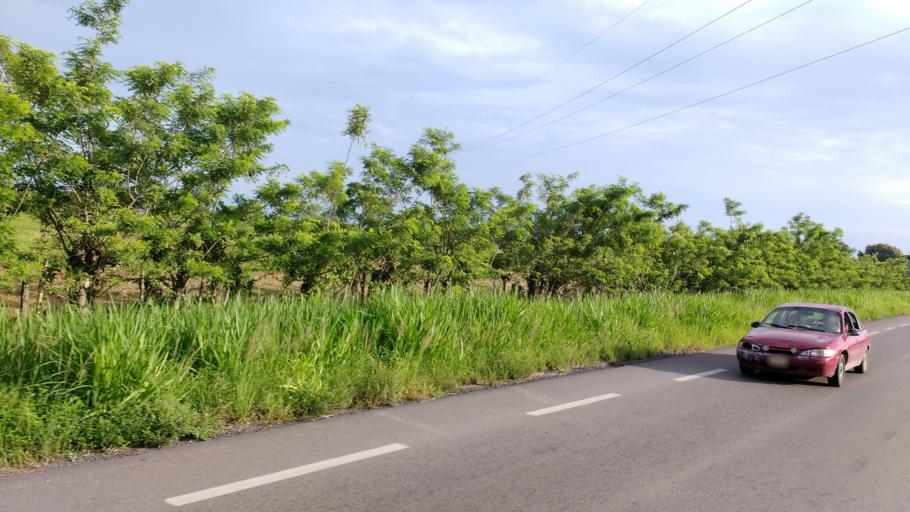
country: MX
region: Tabasco
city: Teapa
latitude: 17.5965
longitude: -92.9636
